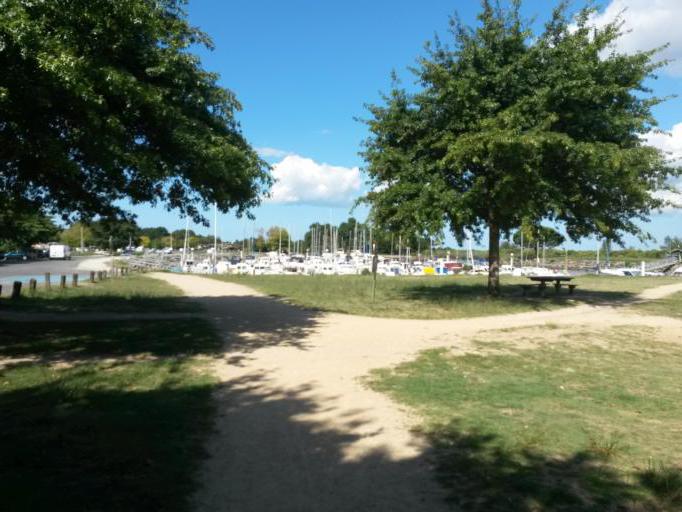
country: FR
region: Aquitaine
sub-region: Departement de la Gironde
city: Le Teich
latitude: 44.6399
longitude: -1.0161
